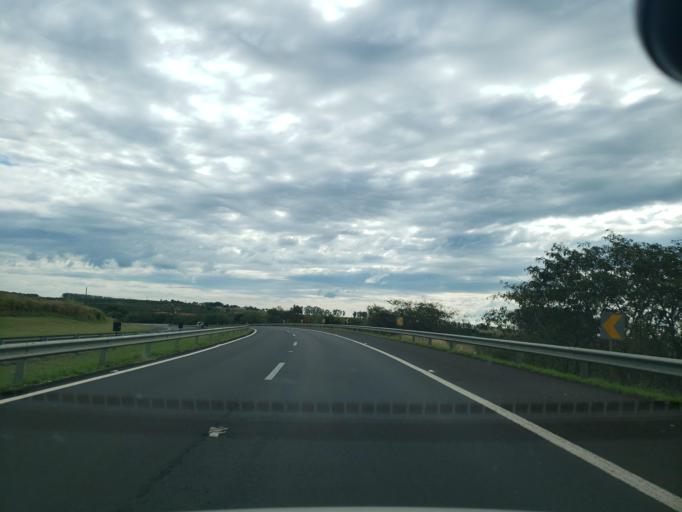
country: BR
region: Sao Paulo
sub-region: Bauru
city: Bauru
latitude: -22.1978
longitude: -49.1881
